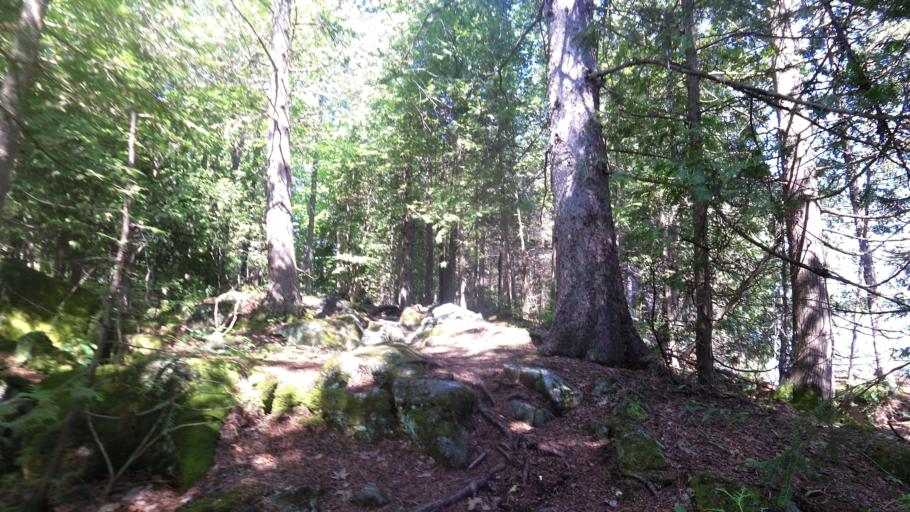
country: CA
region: Ontario
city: Arnprior
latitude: 45.4643
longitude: -76.2645
